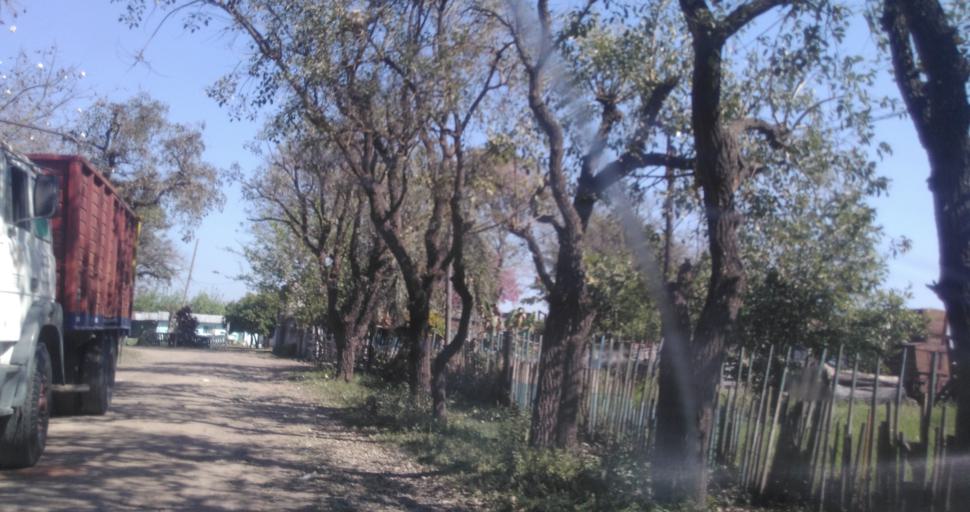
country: AR
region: Chaco
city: Fontana
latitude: -27.4315
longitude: -59.0311
